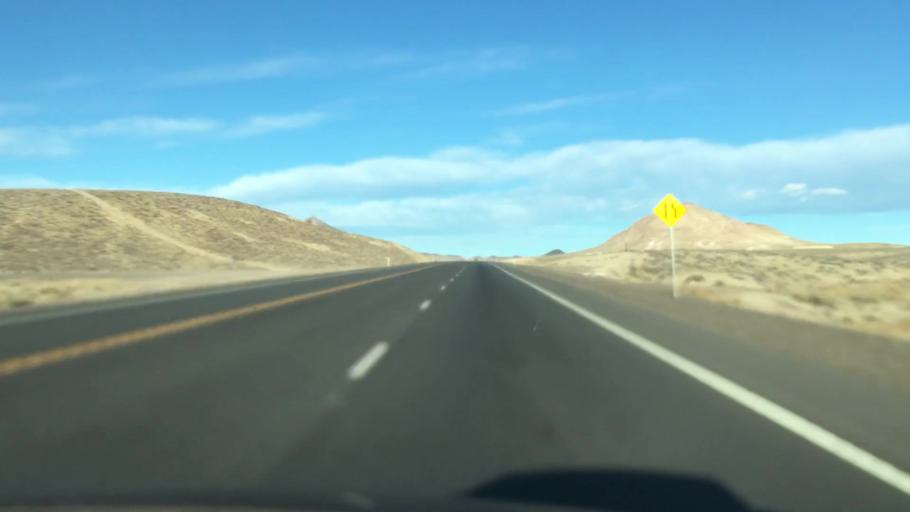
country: US
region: Nevada
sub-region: Nye County
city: Tonopah
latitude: 38.0062
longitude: -117.2607
